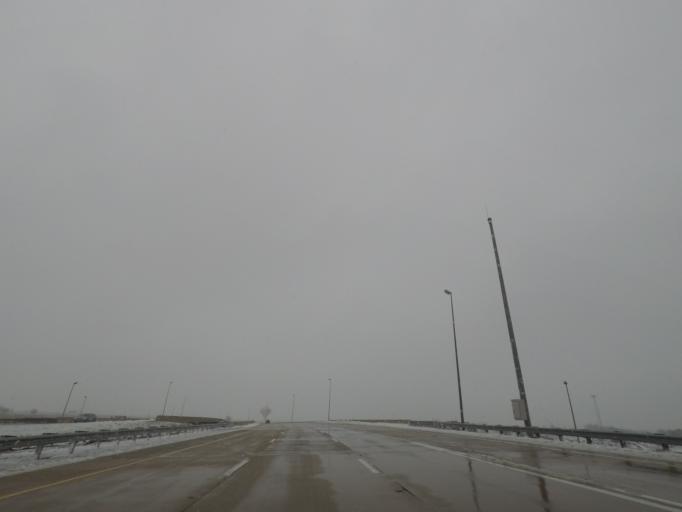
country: US
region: Illinois
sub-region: McLean County
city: Normal
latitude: 40.5378
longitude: -88.9499
